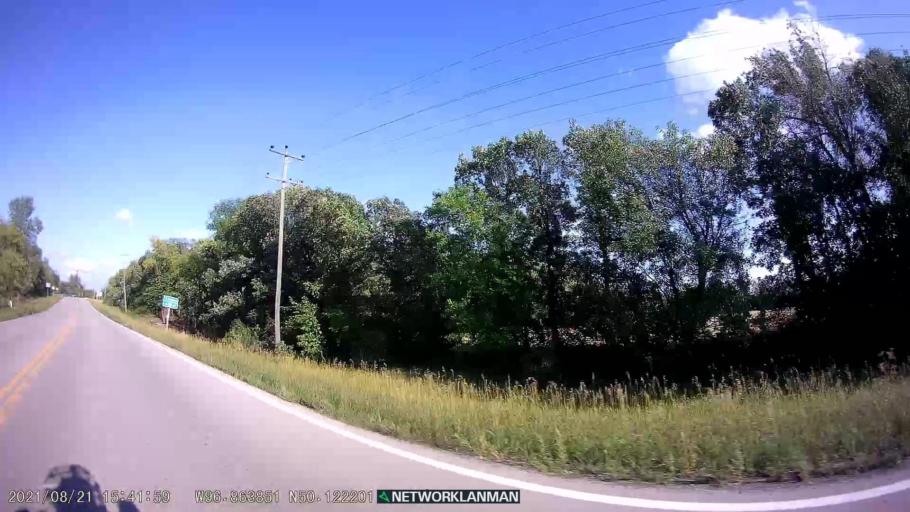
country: CA
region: Manitoba
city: Selkirk
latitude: 50.1222
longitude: -96.8634
